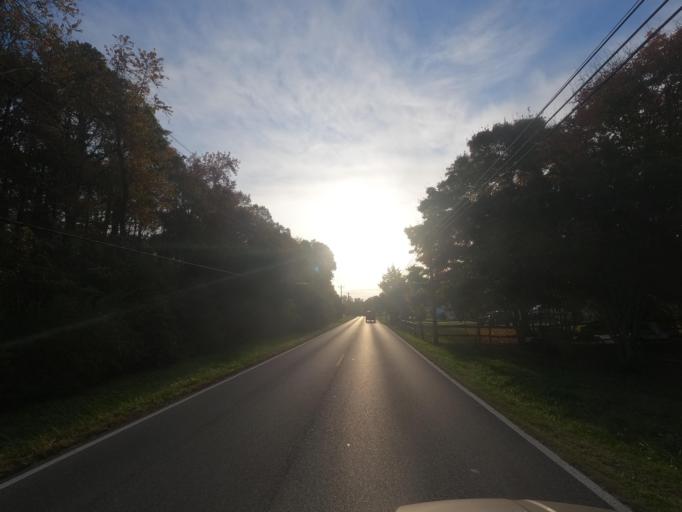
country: US
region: Maryland
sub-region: Calvert County
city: Lusby
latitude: 38.3873
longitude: -76.4285
